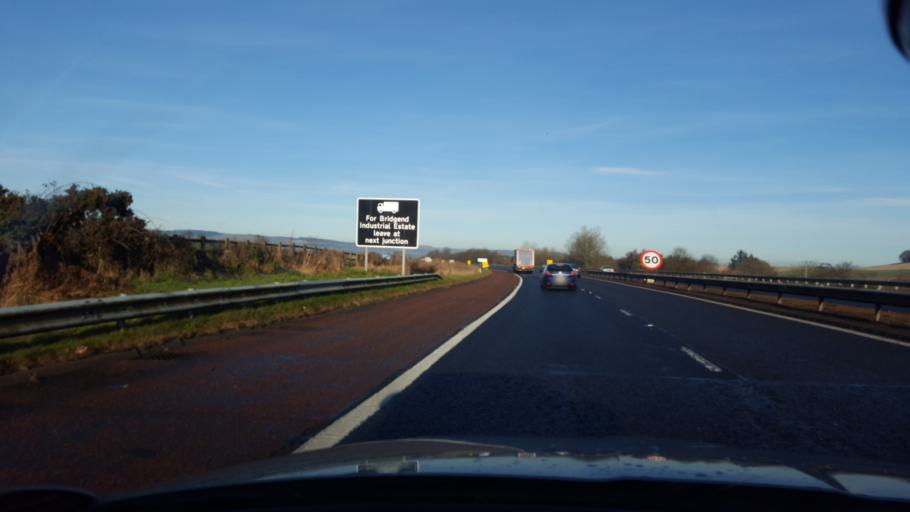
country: GB
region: Scotland
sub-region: Fife
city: Kelty
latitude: 56.1496
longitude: -3.3935
